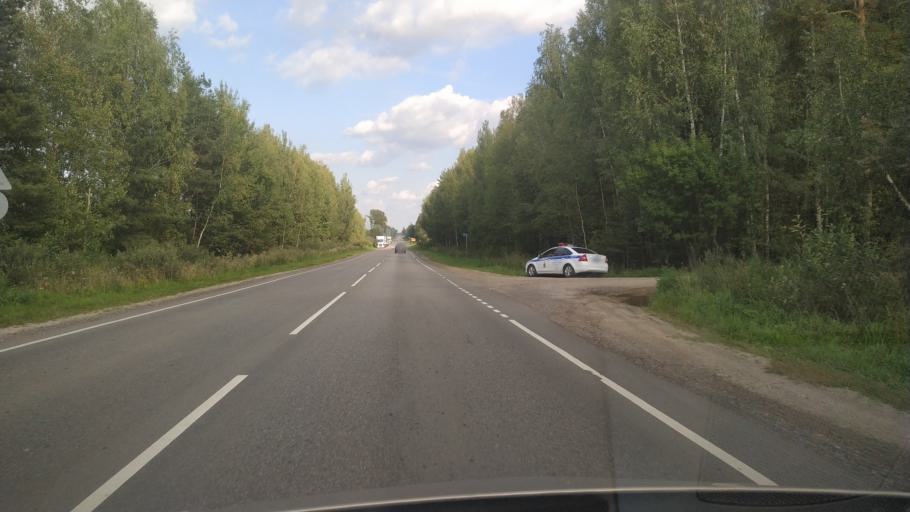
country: RU
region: Moskovskaya
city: Vereya
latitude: 55.7087
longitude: 39.0862
